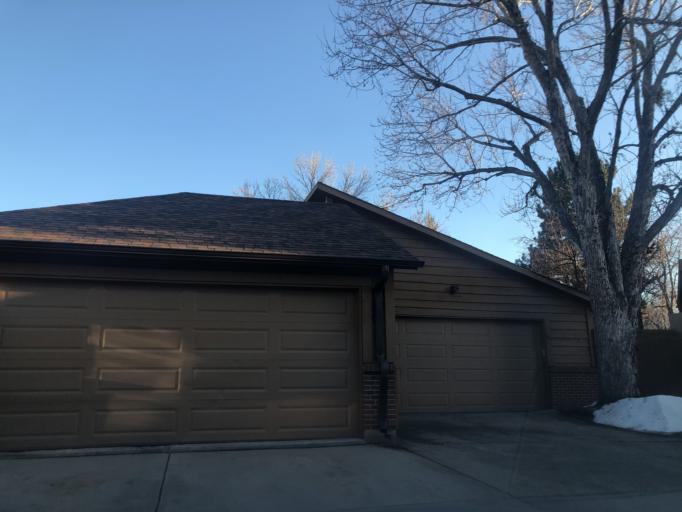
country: US
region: Colorado
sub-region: Adams County
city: Aurora
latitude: 39.7160
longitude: -104.8164
